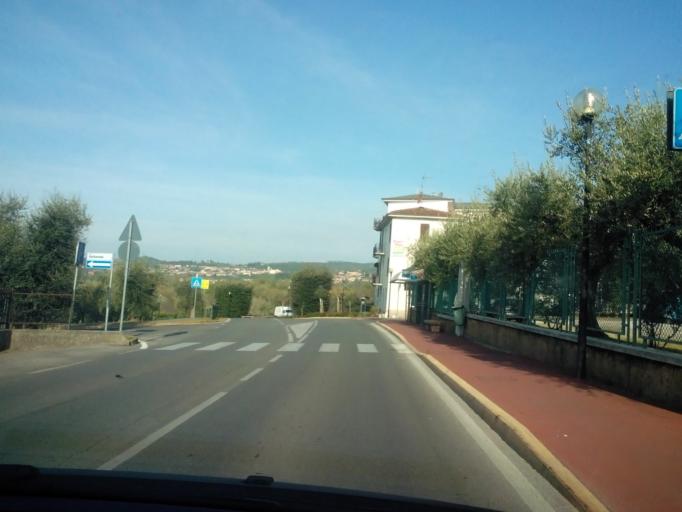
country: IT
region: Lombardy
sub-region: Provincia di Brescia
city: Manerba del Garda
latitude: 45.5496
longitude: 10.5426
